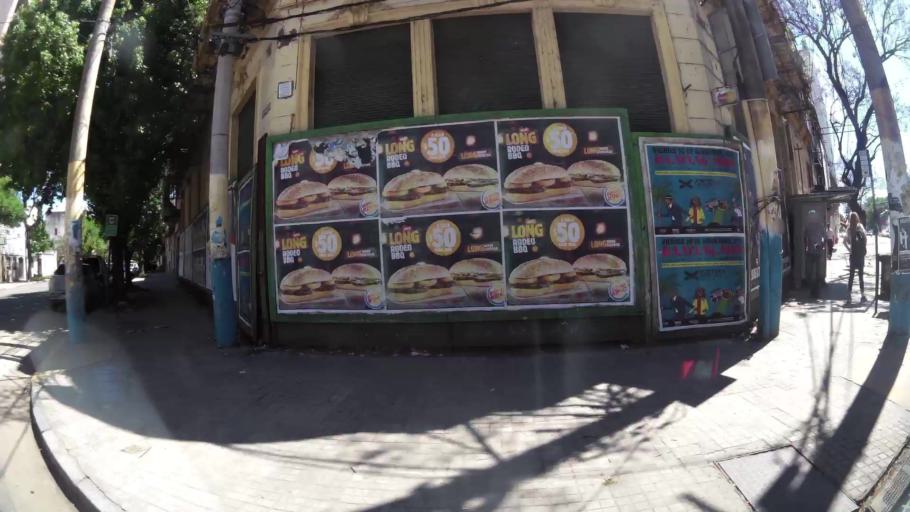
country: AR
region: Santa Fe
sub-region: Departamento de Rosario
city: Rosario
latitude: -32.9336
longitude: -60.6693
